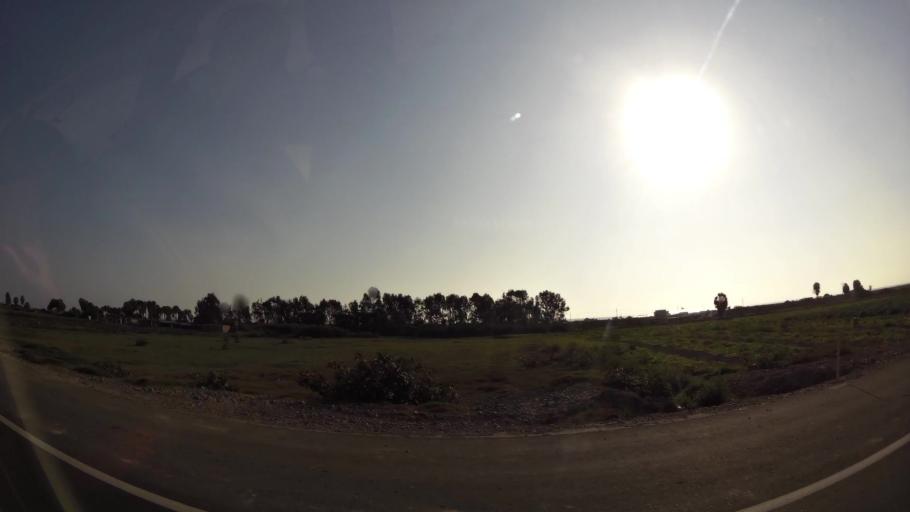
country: PE
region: Ica
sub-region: Provincia de Chincha
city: Chincha Baja
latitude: -13.5395
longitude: -76.1829
